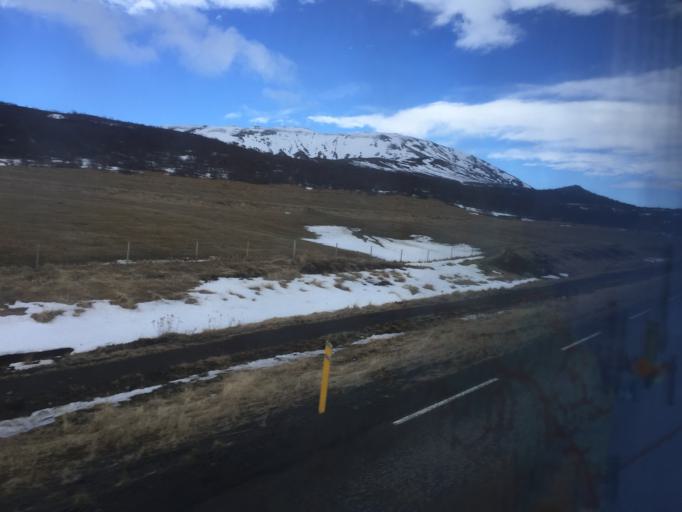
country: IS
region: South
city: Selfoss
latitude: 64.2239
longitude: -20.6094
